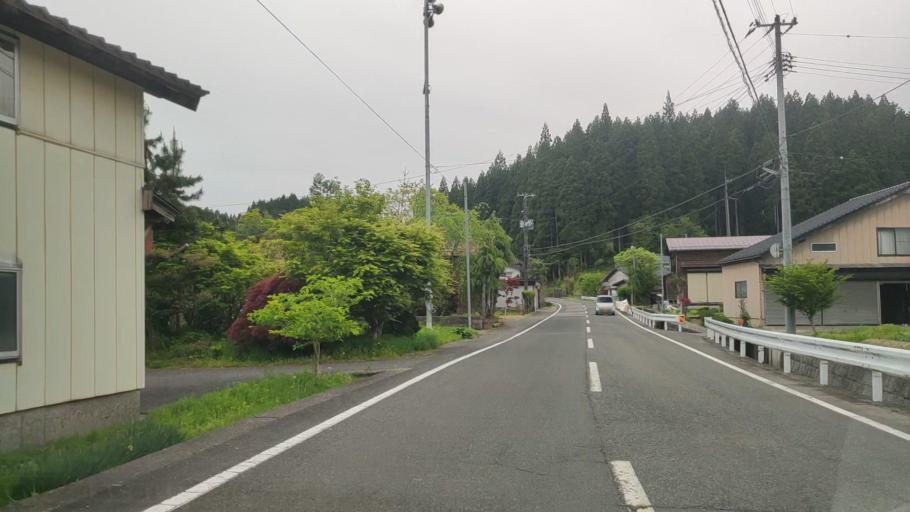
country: JP
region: Niigata
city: Gosen
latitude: 37.7232
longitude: 139.1302
